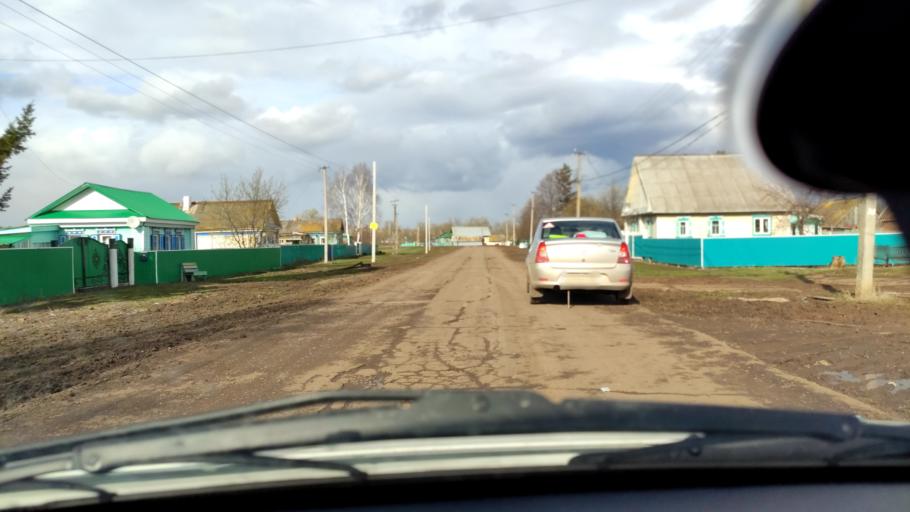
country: RU
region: Bashkortostan
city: Buzdyak
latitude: 54.7661
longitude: 54.6206
